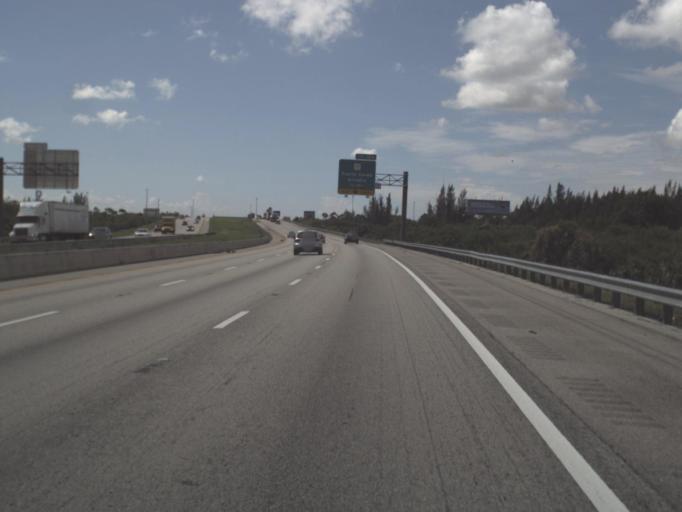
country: US
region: Florida
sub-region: Charlotte County
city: Punta Gorda
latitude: 26.9476
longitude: -82.0210
